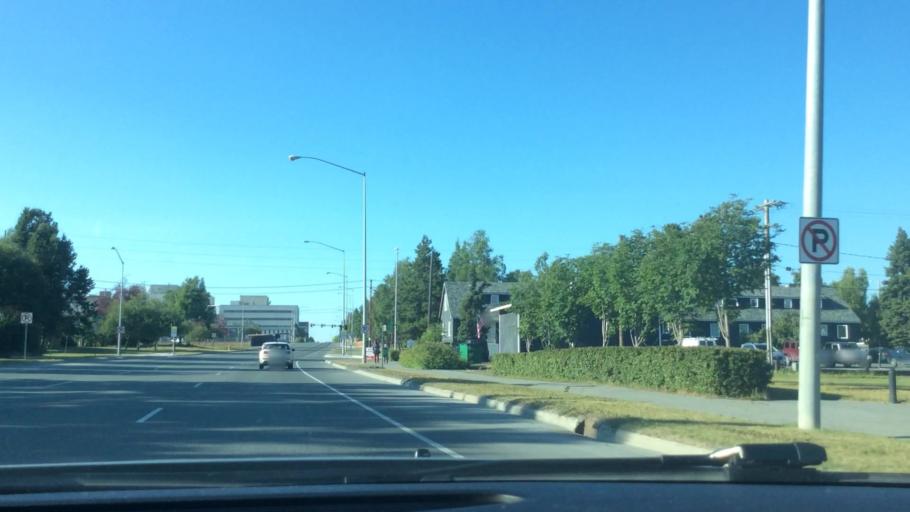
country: US
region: Alaska
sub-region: Anchorage Municipality
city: Anchorage
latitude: 61.2107
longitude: -149.8830
